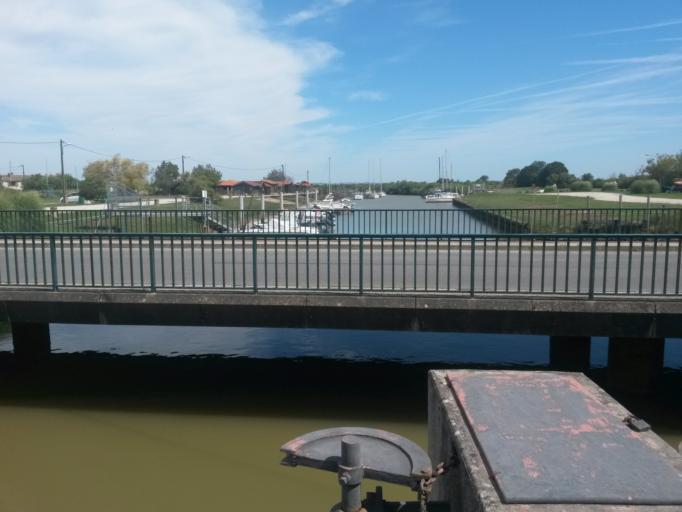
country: FR
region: Aquitaine
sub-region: Departement de la Gironde
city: Gaillan-en-Medoc
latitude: 45.4045
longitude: -0.9107
